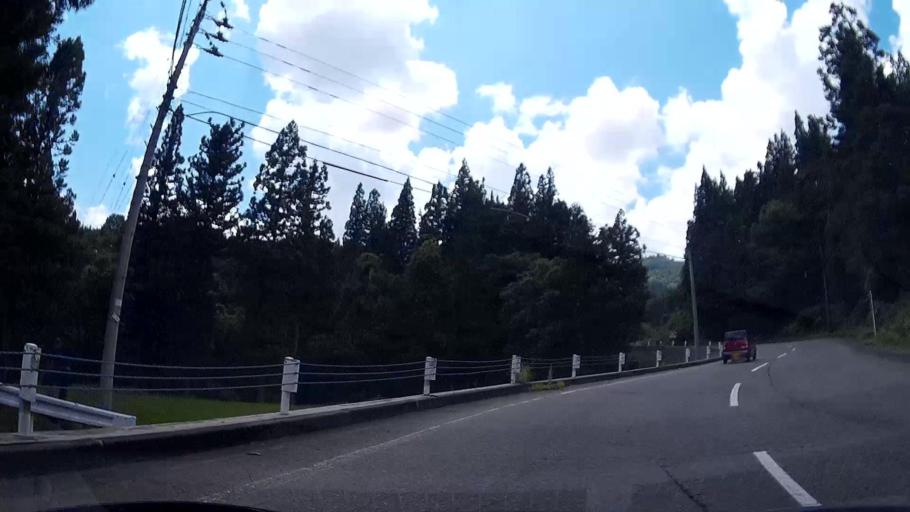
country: JP
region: Niigata
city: Shiozawa
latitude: 37.0209
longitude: 138.8087
